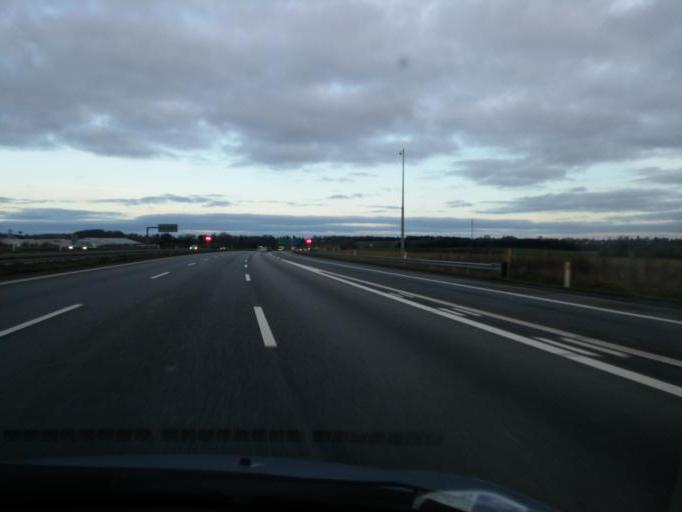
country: DK
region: South Denmark
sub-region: Vejle Kommune
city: Vejle
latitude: 55.6654
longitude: 9.5545
